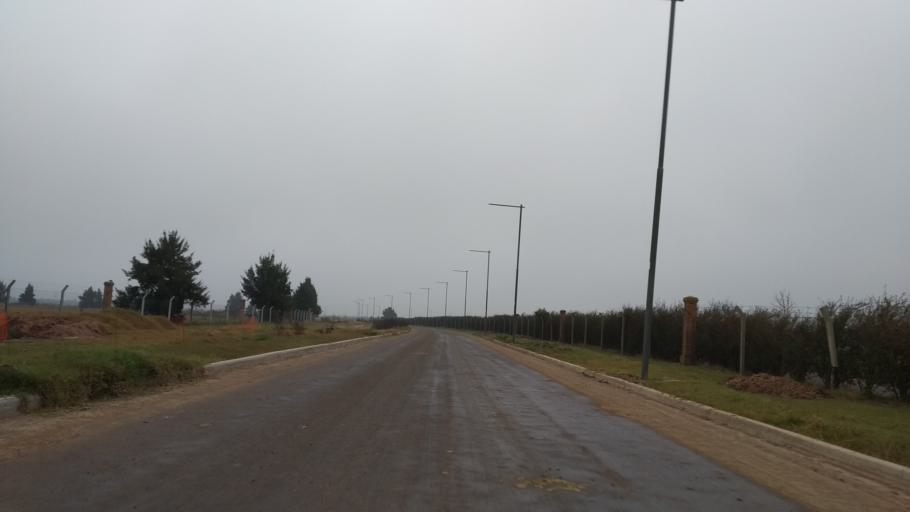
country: AR
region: Santa Fe
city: Funes
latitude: -32.9412
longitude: -60.7665
